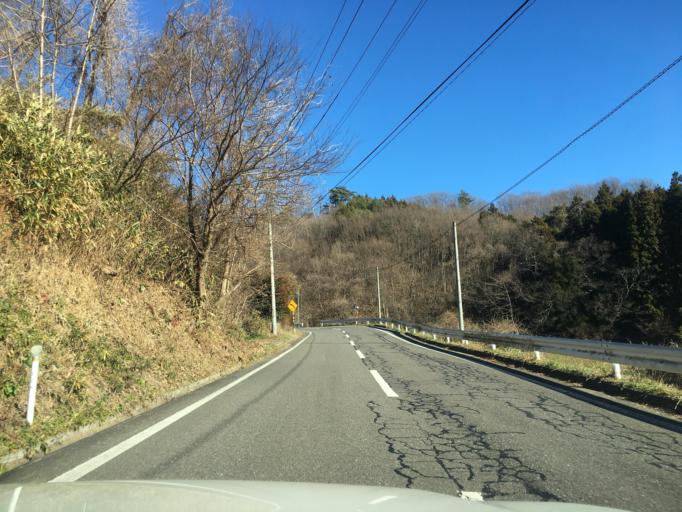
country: JP
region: Fukushima
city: Miharu
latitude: 37.4555
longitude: 140.4639
